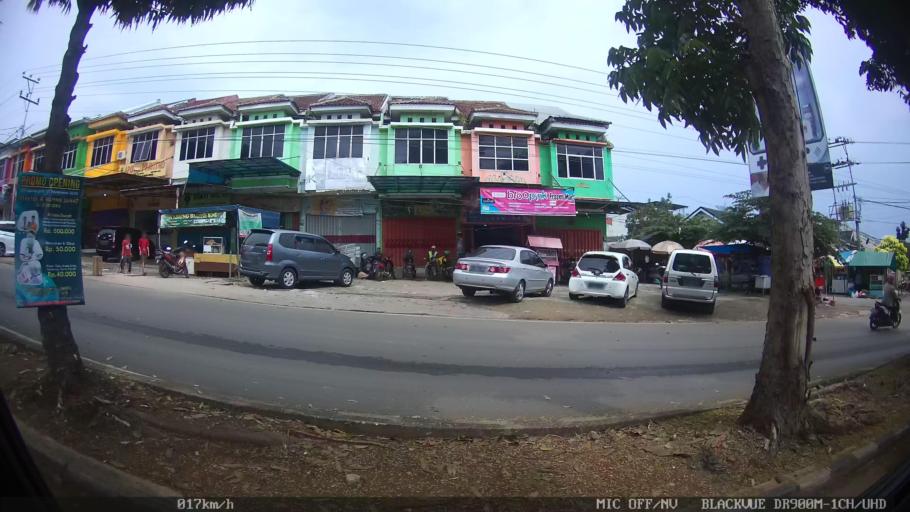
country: ID
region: Lampung
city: Kedaton
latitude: -5.3980
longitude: 105.2039
